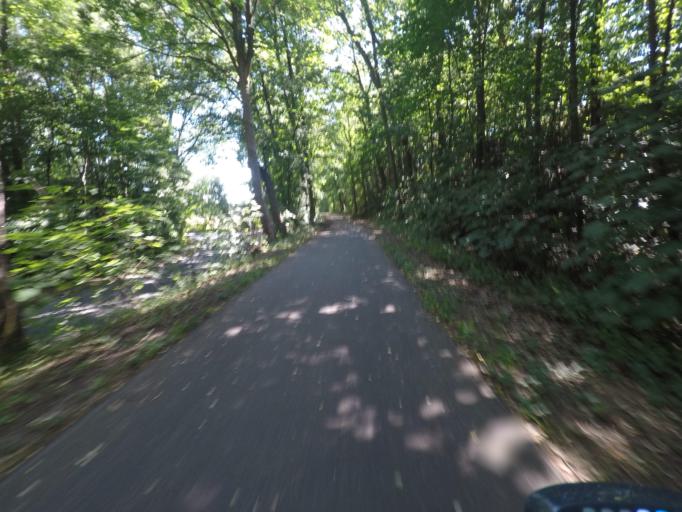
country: DE
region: Schleswig-Holstein
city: Lutjensee
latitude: 53.6389
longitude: 10.3737
